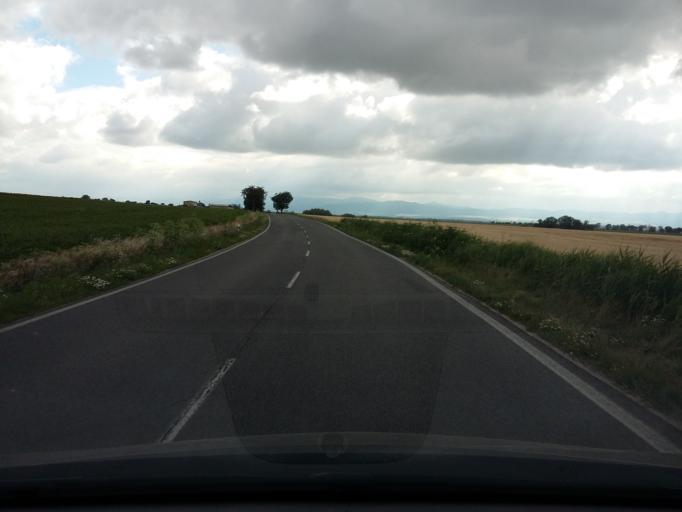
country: SK
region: Trnavsky
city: Vrbove
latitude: 48.6010
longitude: 17.6990
